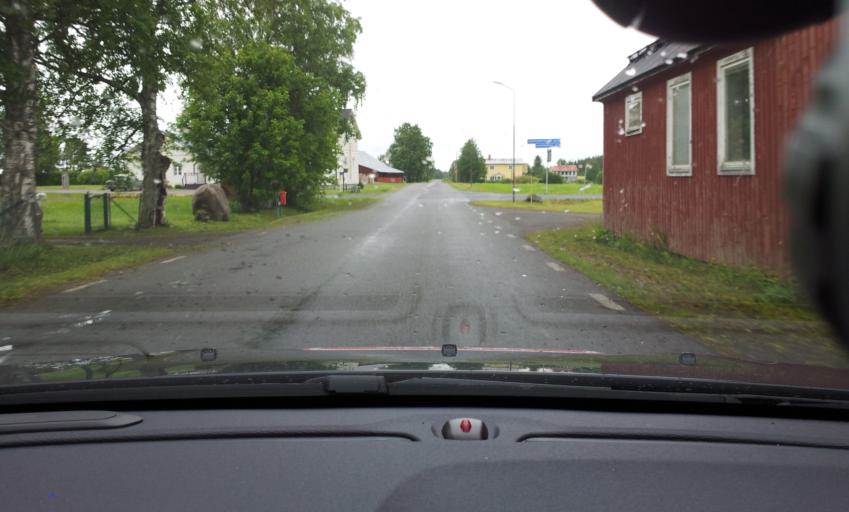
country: SE
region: Jaemtland
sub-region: OEstersunds Kommun
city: Lit
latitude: 63.6743
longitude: 15.1043
